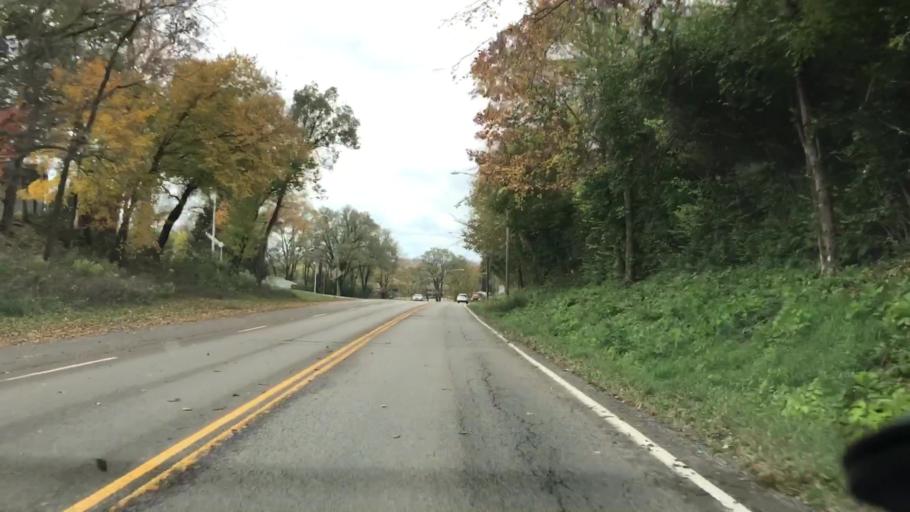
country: US
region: Ohio
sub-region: Greene County
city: Fairborn
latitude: 39.8364
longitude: -84.0105
